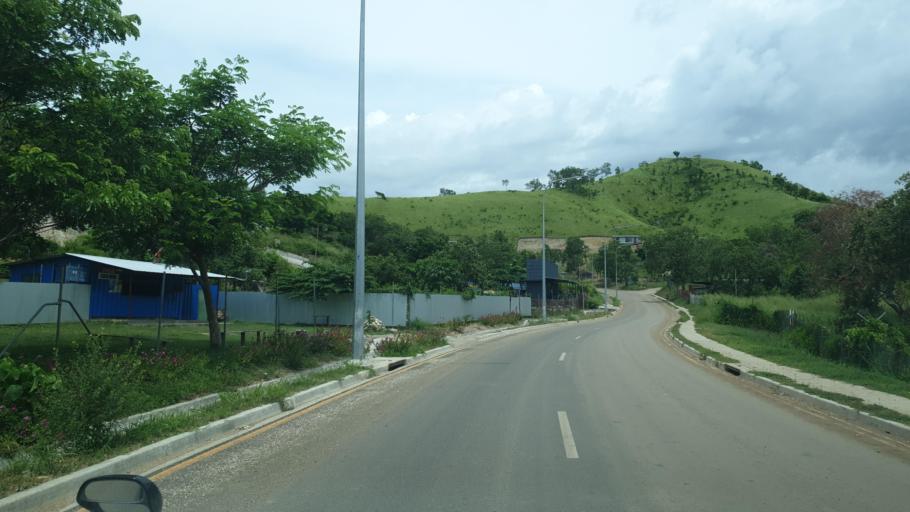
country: PG
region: National Capital
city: Port Moresby
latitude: -9.5274
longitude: 147.2481
